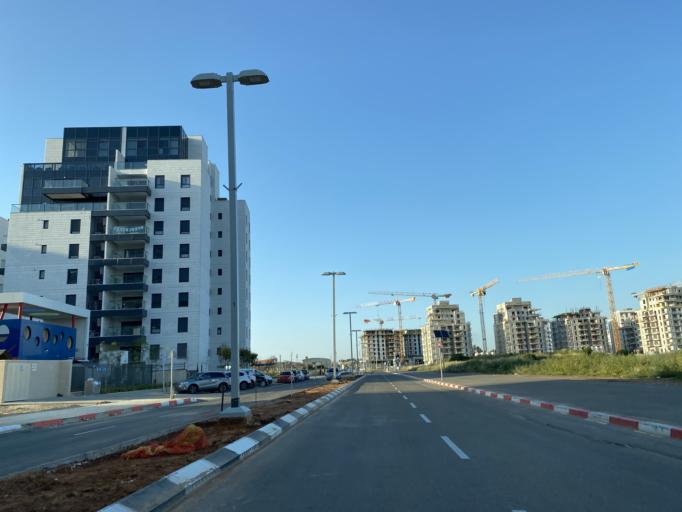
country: IL
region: Tel Aviv
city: Herzliyya
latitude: 32.1584
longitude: 34.8230
